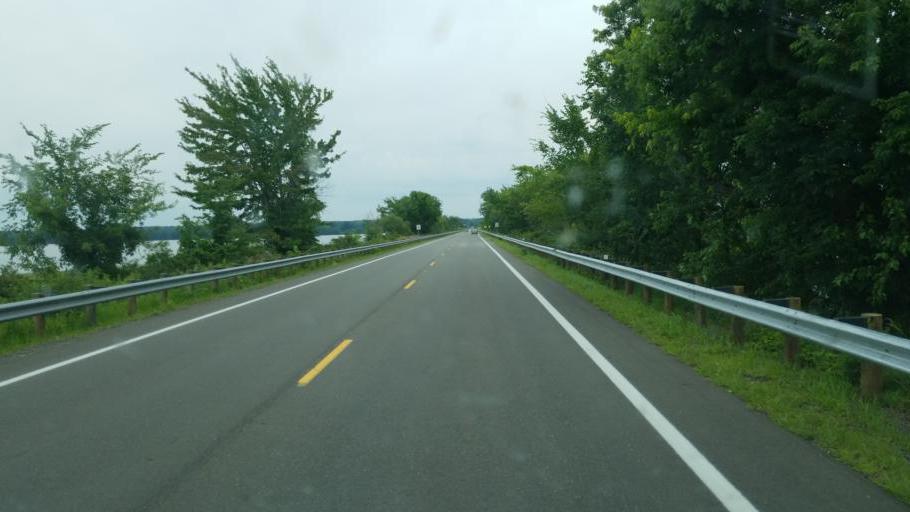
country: US
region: Ohio
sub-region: Trumbull County
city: Cortland
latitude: 41.3900
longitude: -80.7606
